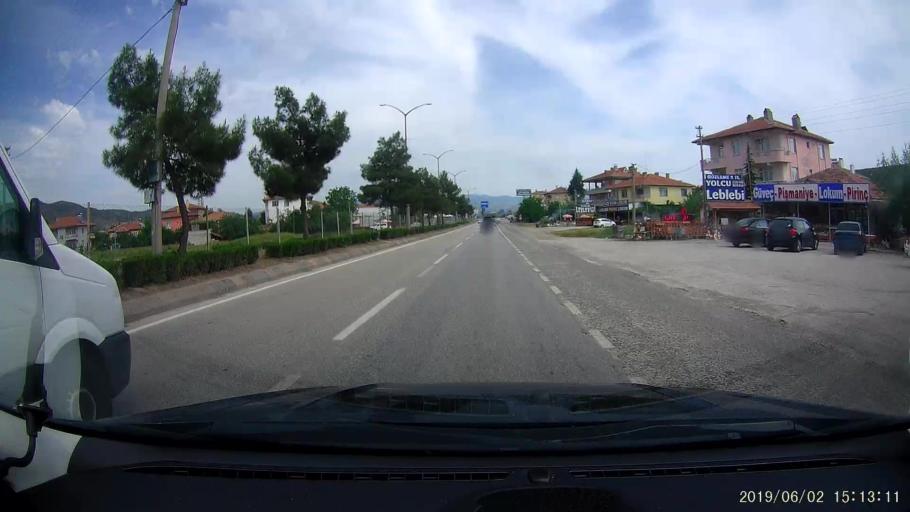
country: TR
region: Corum
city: Osmancik
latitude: 40.9734
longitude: 34.8187
